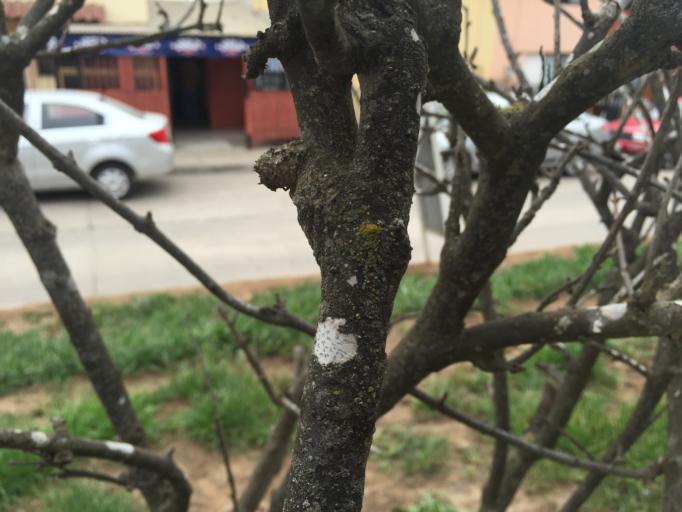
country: CL
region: Coquimbo
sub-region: Provincia de Elqui
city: La Serena
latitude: -29.9146
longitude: -71.2447
